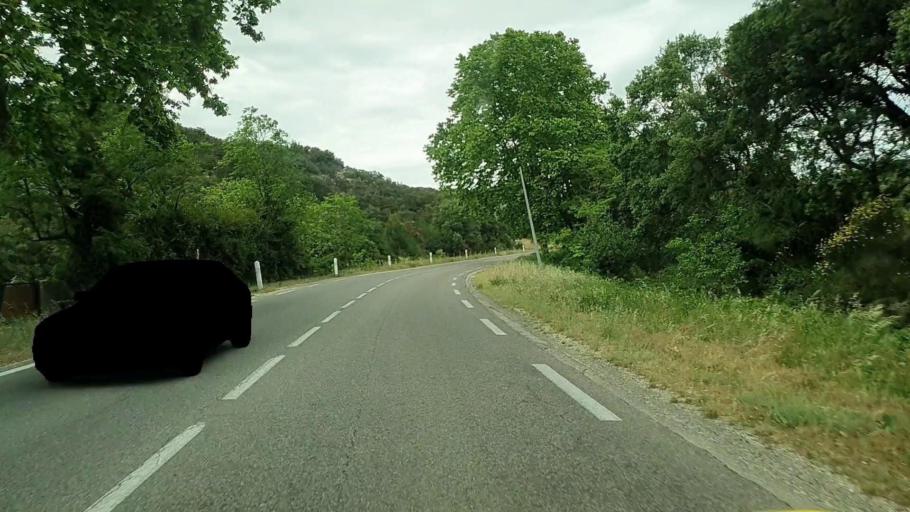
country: FR
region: Languedoc-Roussillon
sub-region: Departement du Gard
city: Castillon-du-Gard
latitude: 43.9948
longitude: 4.5772
